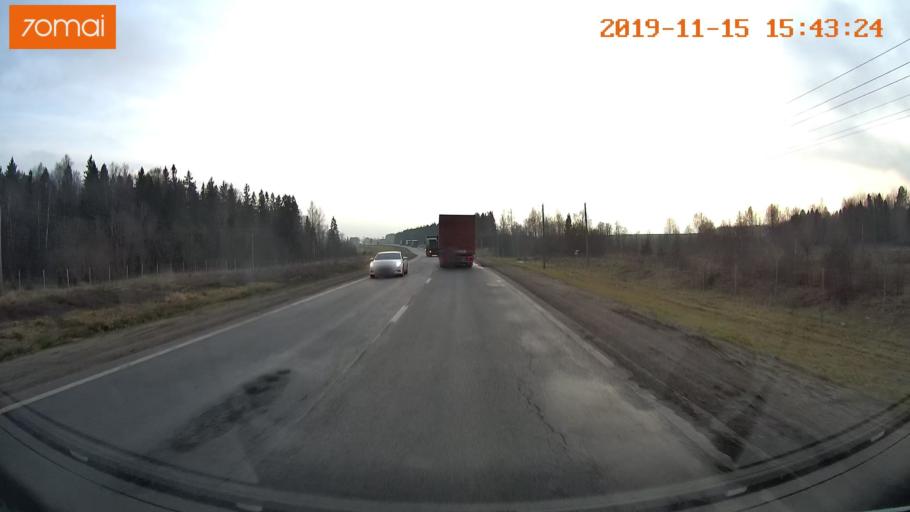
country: RU
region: Jaroslavl
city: Danilov
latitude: 57.9827
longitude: 40.0281
